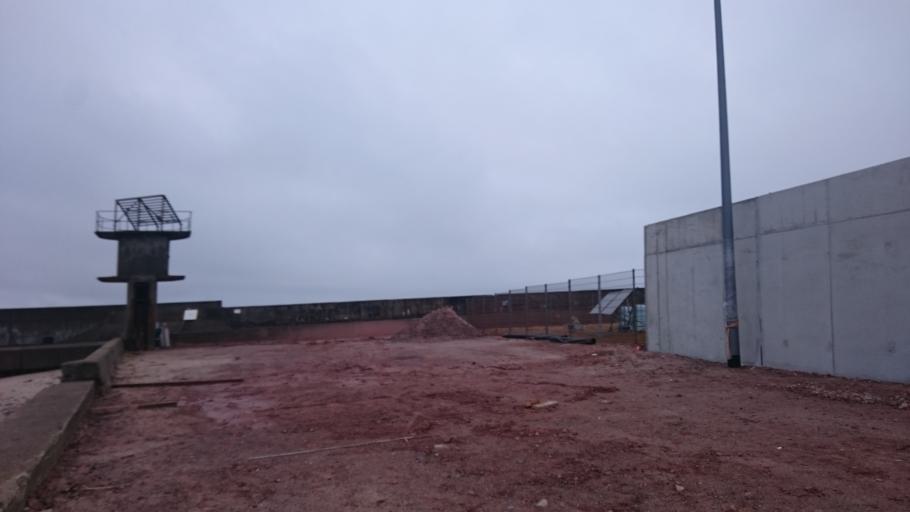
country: DE
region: Schleswig-Holstein
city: Helgoland
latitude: 54.1729
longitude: 7.8903
